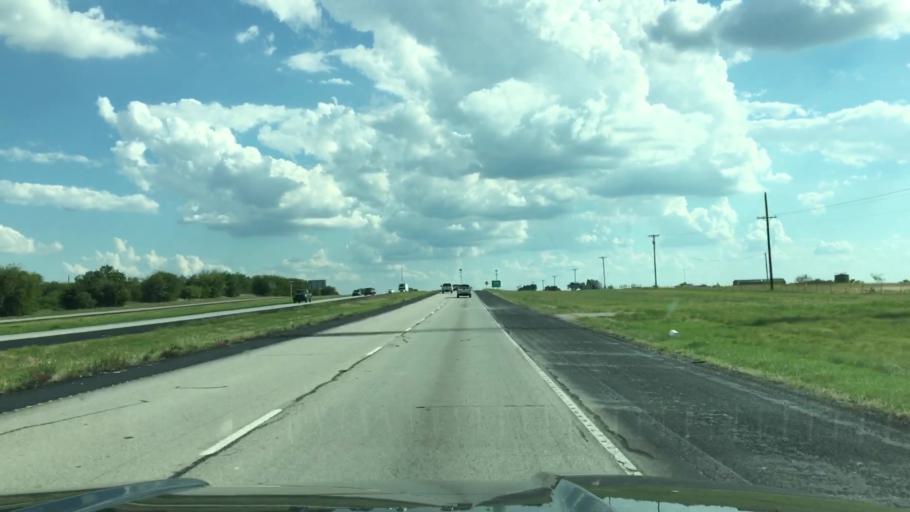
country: US
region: Texas
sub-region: Wise County
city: Rhome
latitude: 33.0766
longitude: -97.4731
